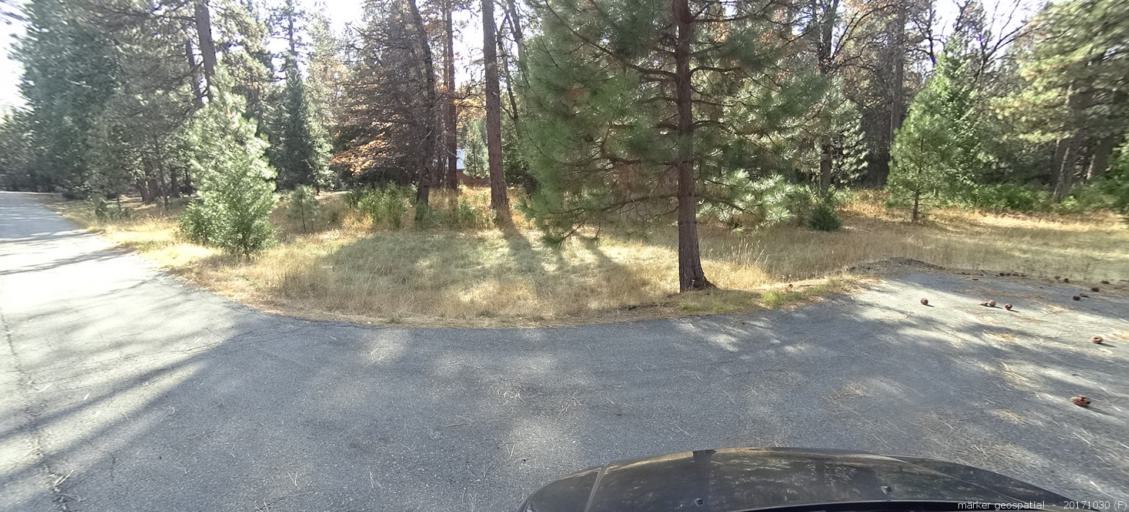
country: US
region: California
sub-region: Shasta County
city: Shingletown
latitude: 40.5244
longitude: -121.6854
